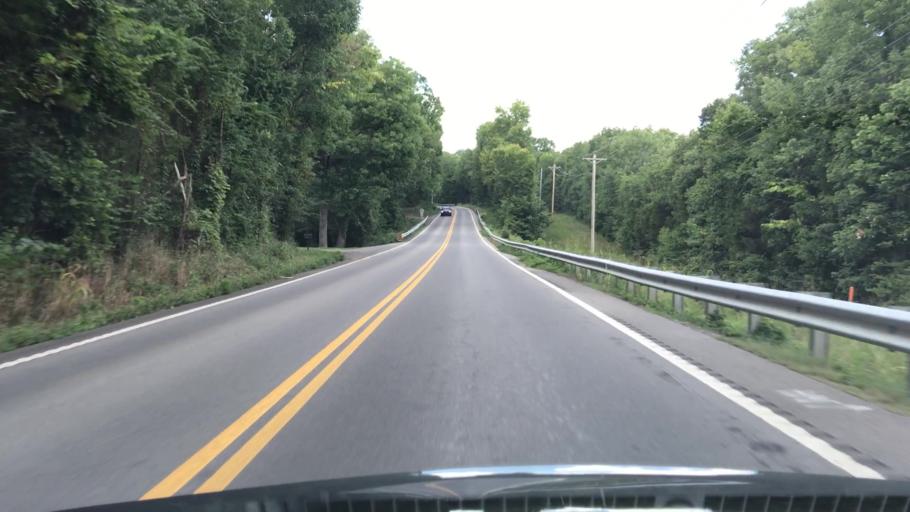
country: US
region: Tennessee
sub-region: Williamson County
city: Nolensville
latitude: 35.8516
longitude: -86.6015
